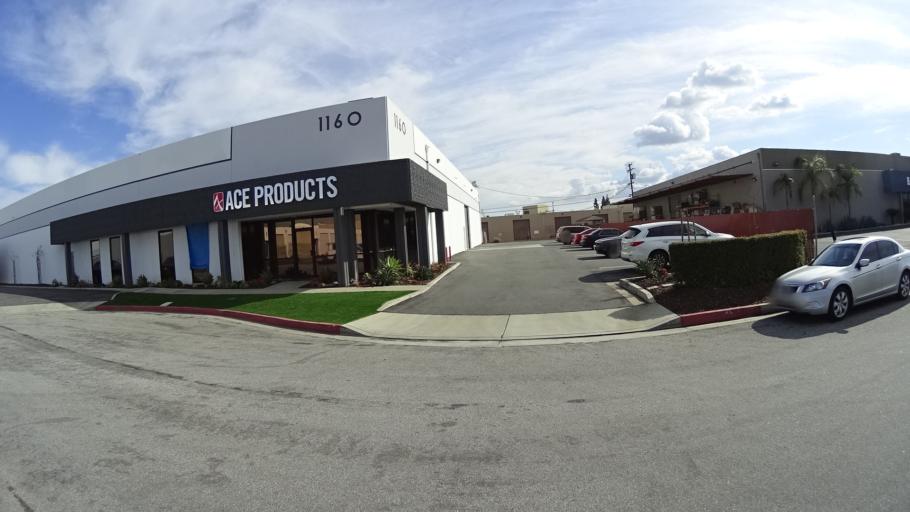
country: US
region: California
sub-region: Orange County
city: Placentia
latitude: 33.8557
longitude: -117.8452
